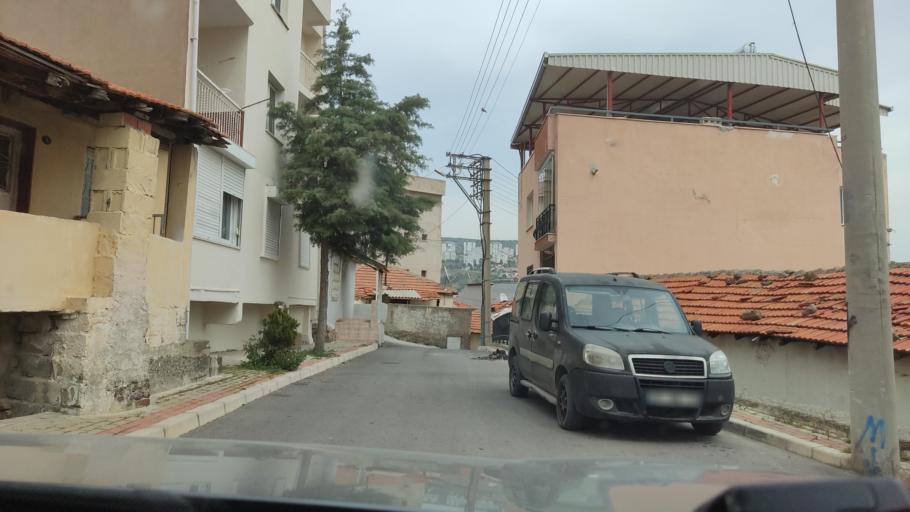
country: TR
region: Izmir
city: Karsiyaka
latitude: 38.4989
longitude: 27.0753
